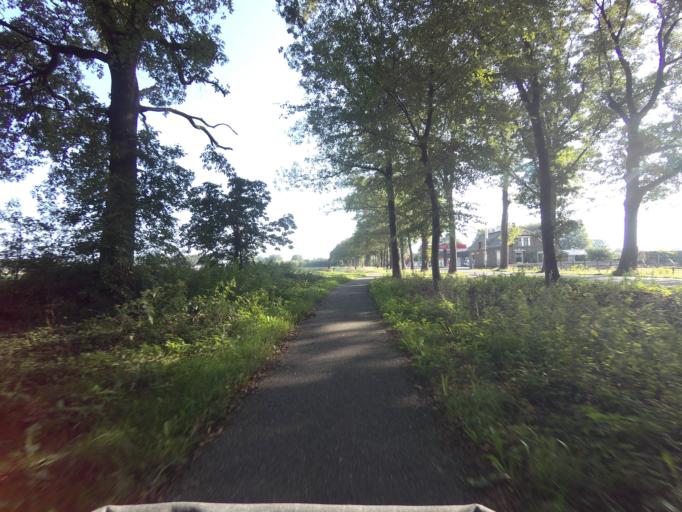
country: NL
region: Overijssel
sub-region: Gemeente Deventer
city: Schalkhaar
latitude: 52.2974
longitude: 6.2619
